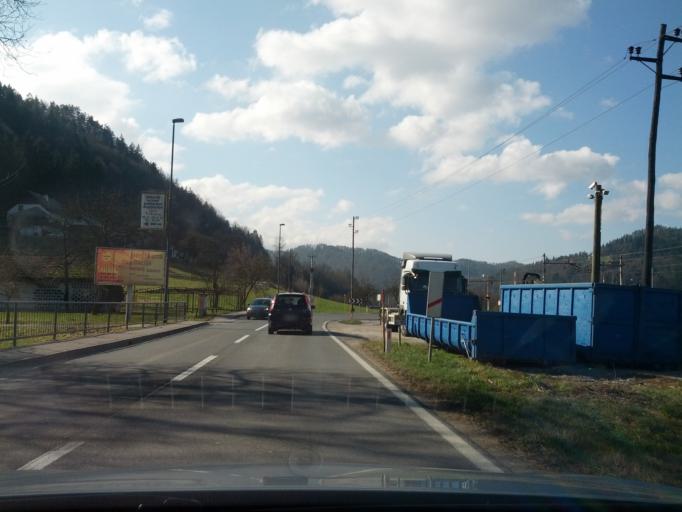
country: SI
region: Litija
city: Litija
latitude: 46.0760
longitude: 14.8246
